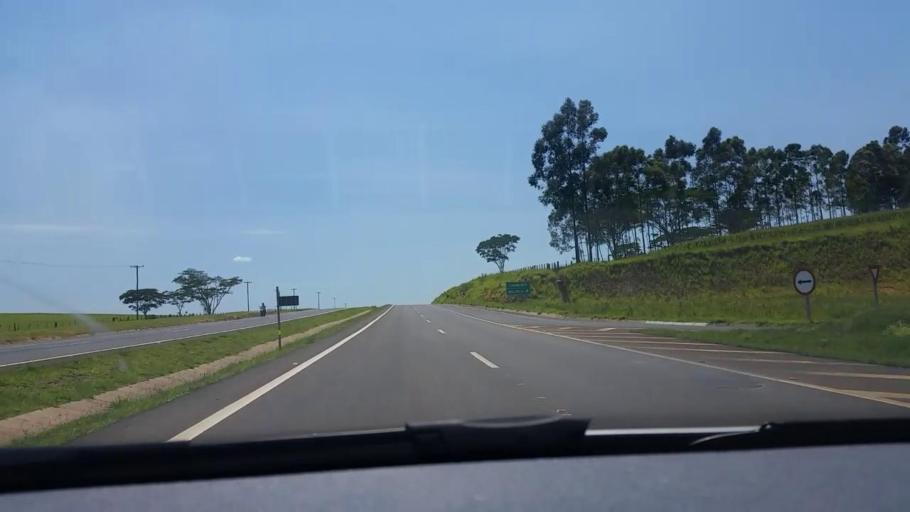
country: BR
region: Sao Paulo
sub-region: Bauru
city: Bauru
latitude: -22.4234
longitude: -49.1227
